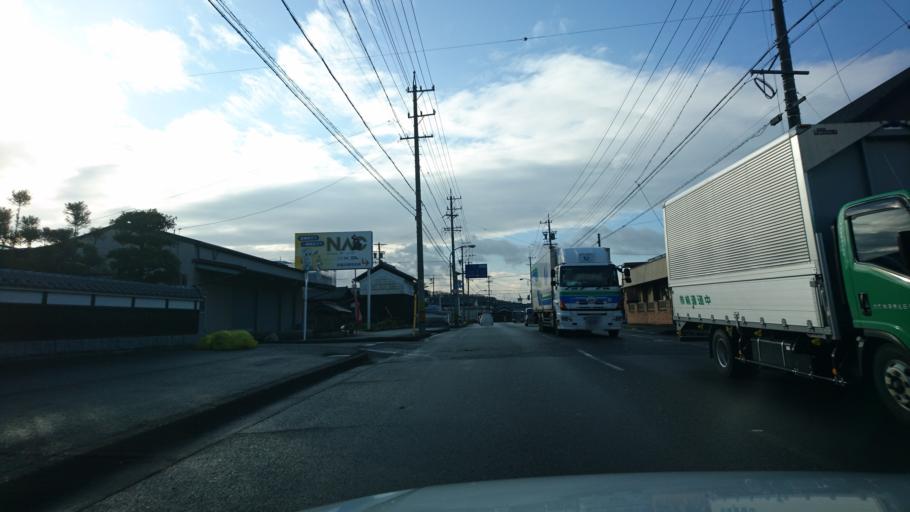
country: JP
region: Mie
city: Ueno-ebisumachi
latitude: 34.7580
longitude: 136.1239
